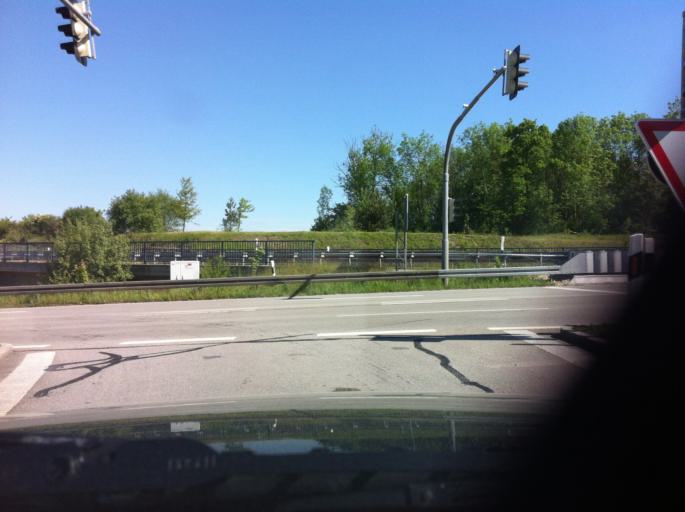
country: DE
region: Bavaria
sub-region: Upper Bavaria
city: Ottobrunn
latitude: 48.0413
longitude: 11.6516
